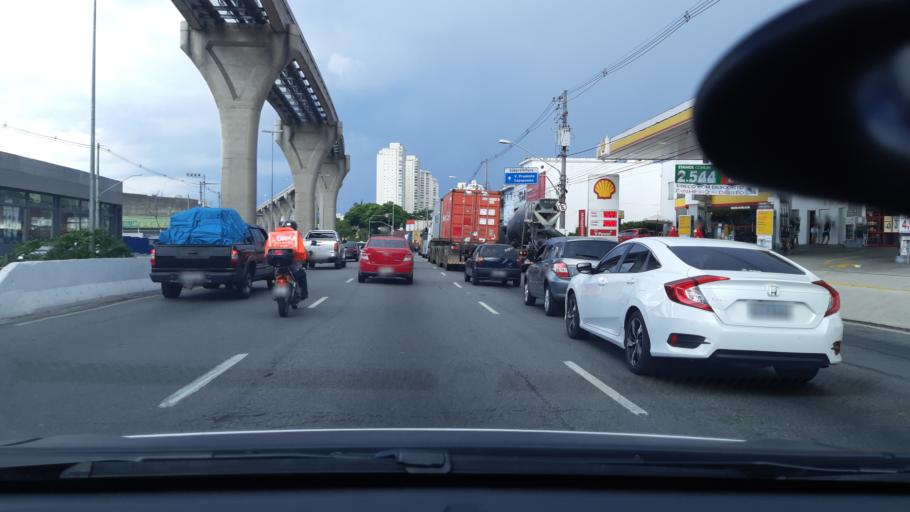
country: BR
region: Sao Paulo
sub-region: Sao Caetano Do Sul
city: Sao Caetano do Sul
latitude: -23.5845
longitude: -46.5782
